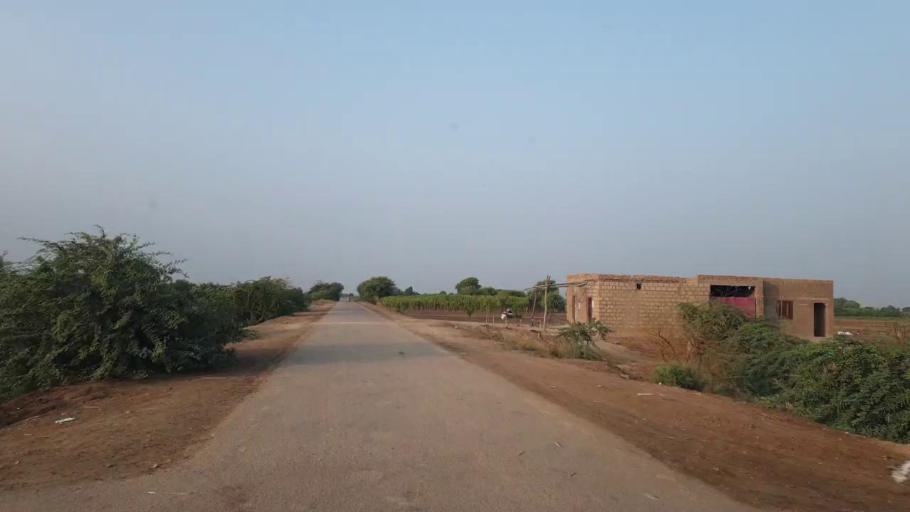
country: PK
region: Sindh
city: Tando Ghulam Ali
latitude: 25.0872
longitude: 68.9586
